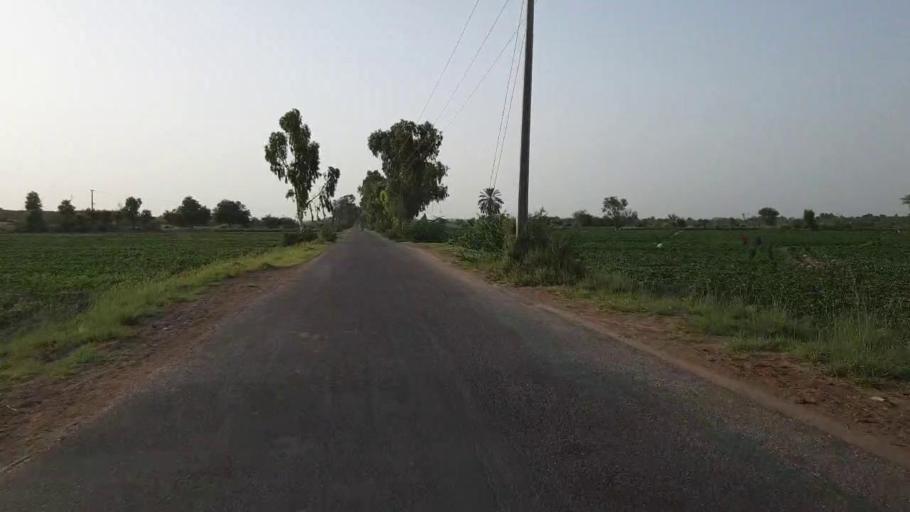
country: PK
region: Sindh
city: Bozdar
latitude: 27.1047
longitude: 68.9619
